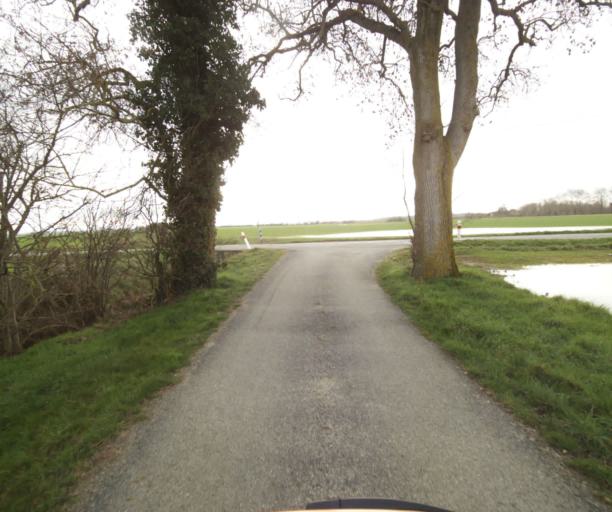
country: FR
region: Midi-Pyrenees
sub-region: Departement de l'Ariege
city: Mazeres
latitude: 43.2205
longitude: 1.7097
